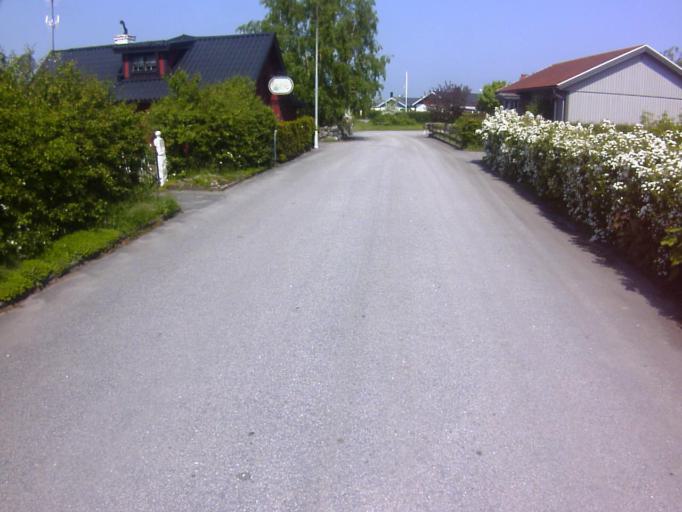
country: SE
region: Blekinge
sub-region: Karlshamns Kommun
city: Morrum
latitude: 56.1179
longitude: 14.6733
